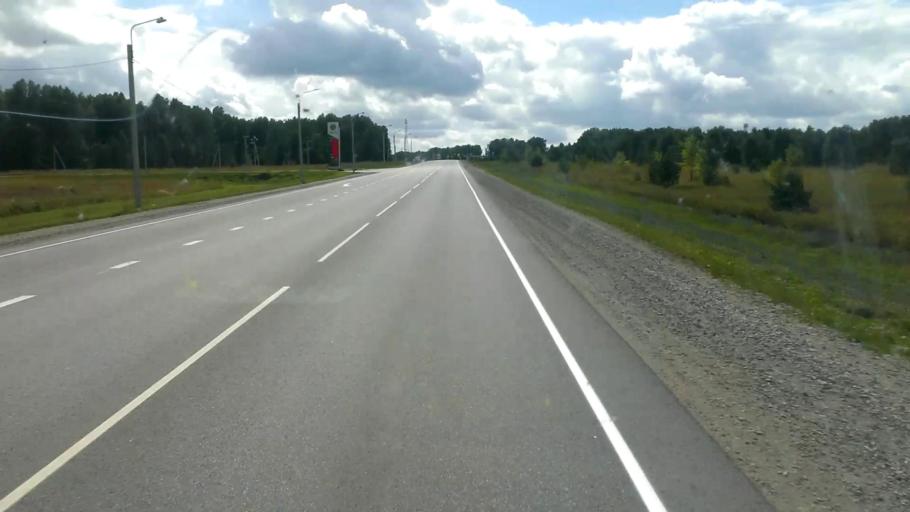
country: RU
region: Altai Krai
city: Troitskoye
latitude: 52.9752
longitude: 84.7468
